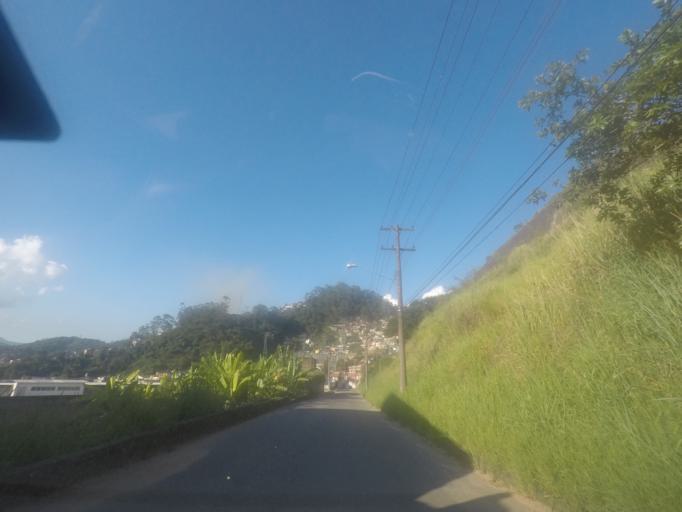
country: BR
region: Rio de Janeiro
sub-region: Petropolis
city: Petropolis
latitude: -22.4883
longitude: -43.1508
